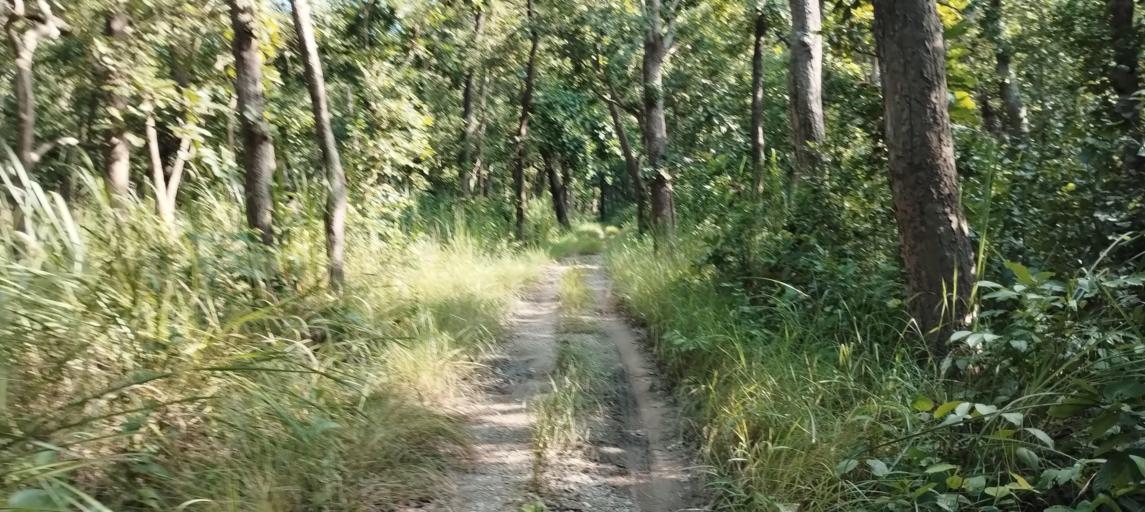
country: NP
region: Far Western
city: Tikapur
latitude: 28.5336
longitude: 81.2831
